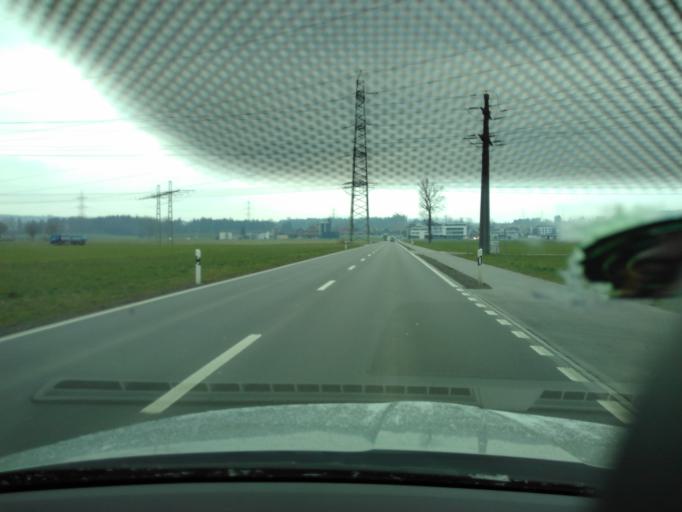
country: CH
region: Lucerne
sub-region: Hochdorf District
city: Inwil
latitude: 47.1148
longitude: 8.3422
